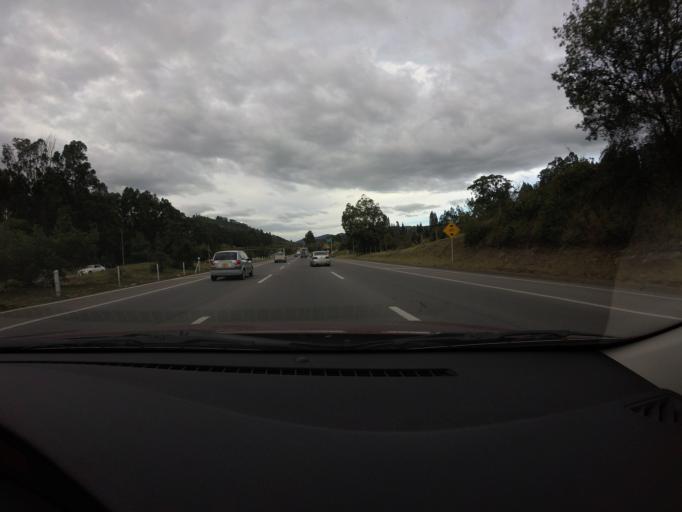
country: CO
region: Cundinamarca
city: Cajica
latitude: 4.9357
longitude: -73.9856
